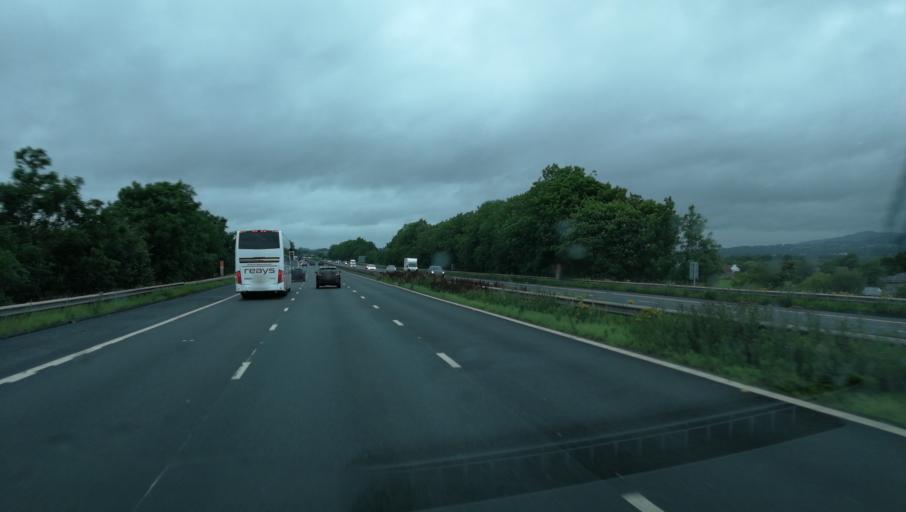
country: GB
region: England
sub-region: Borough of Bolton
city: Westhoughton
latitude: 53.5585
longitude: -2.4988
